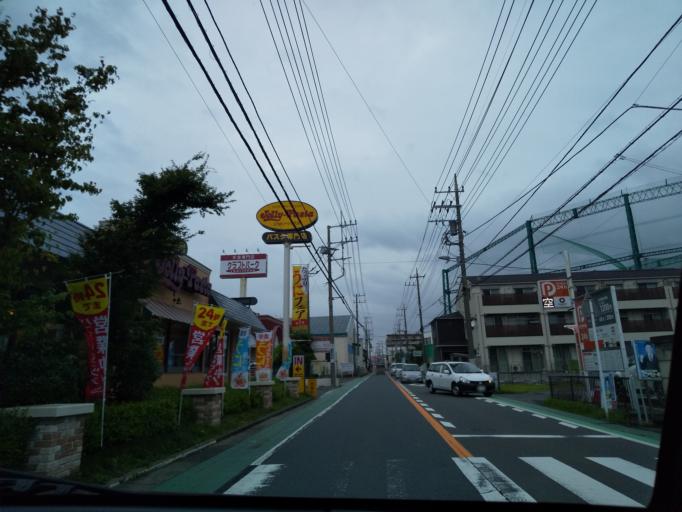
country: JP
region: Kanagawa
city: Fujisawa
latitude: 35.4095
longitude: 139.5005
